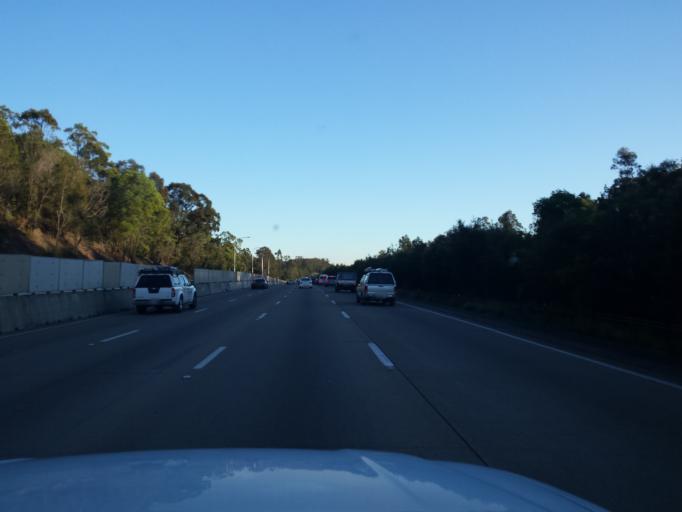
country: AU
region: Queensland
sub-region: Gold Coast
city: Oxenford
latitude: -27.8496
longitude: 153.3066
